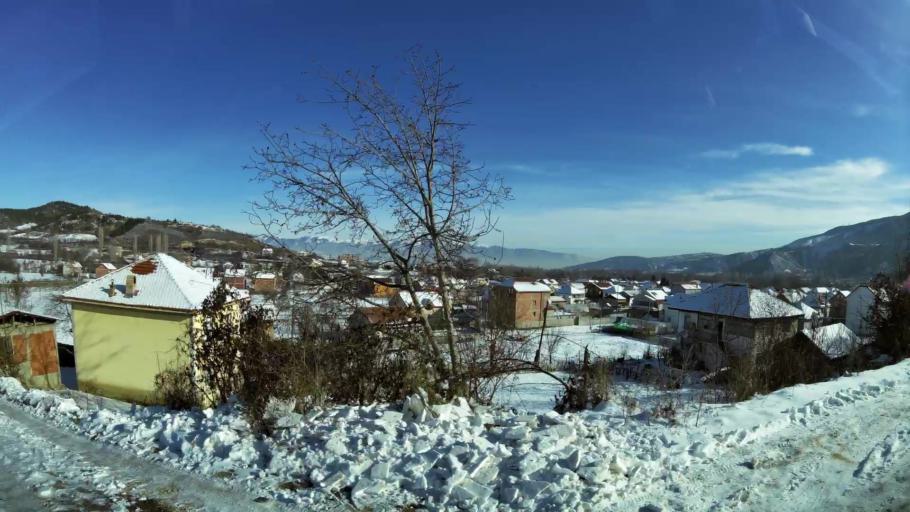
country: MK
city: Ljubin
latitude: 41.9806
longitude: 21.3020
